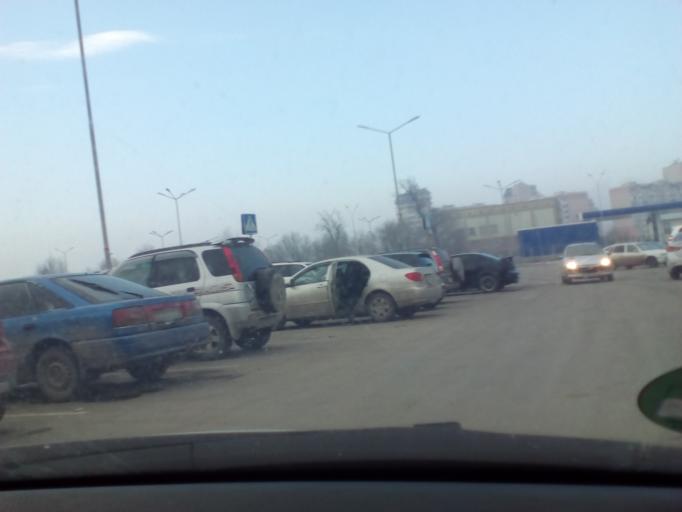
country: KZ
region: Almaty Qalasy
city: Almaty
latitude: 43.2506
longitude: 76.8236
